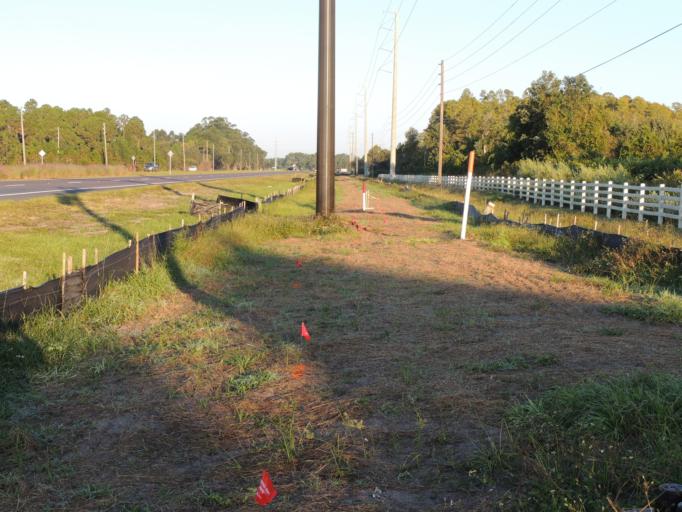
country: US
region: Florida
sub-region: Osceola County
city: Saint Cloud
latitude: 28.1925
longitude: -81.1544
